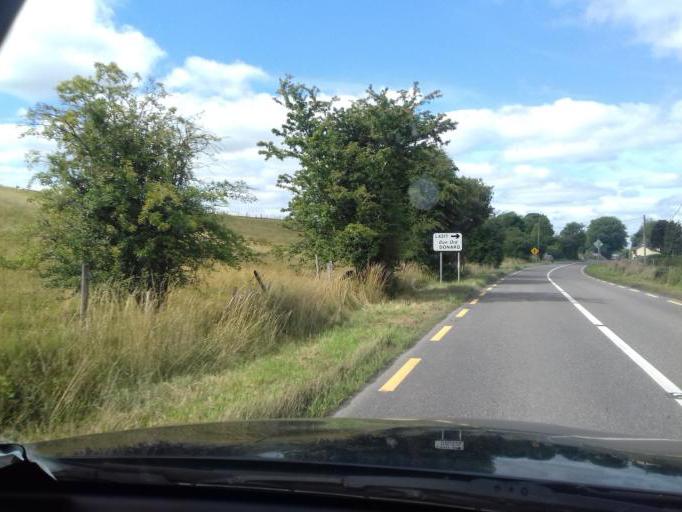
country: IE
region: Leinster
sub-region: Wicklow
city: Valleymount
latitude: 53.0335
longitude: -6.6356
